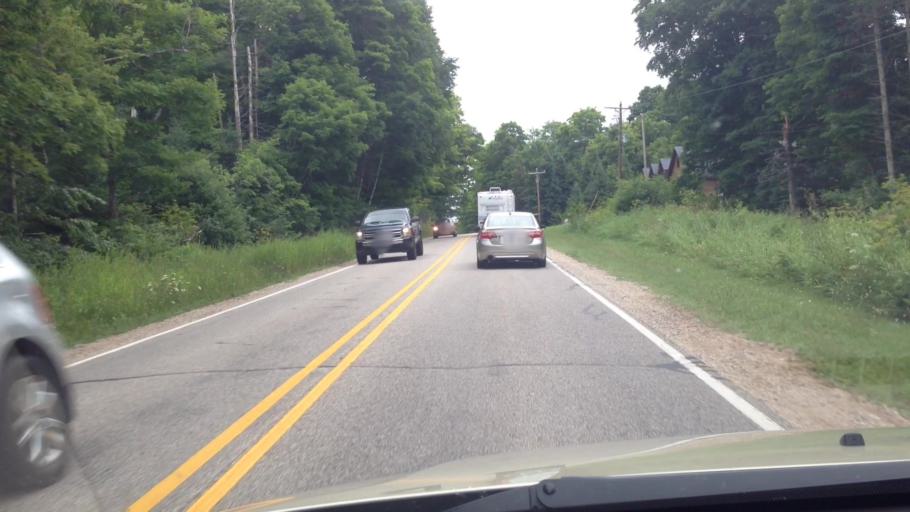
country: US
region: Michigan
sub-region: Mackinac County
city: Saint Ignace
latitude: 46.0511
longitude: -85.1076
